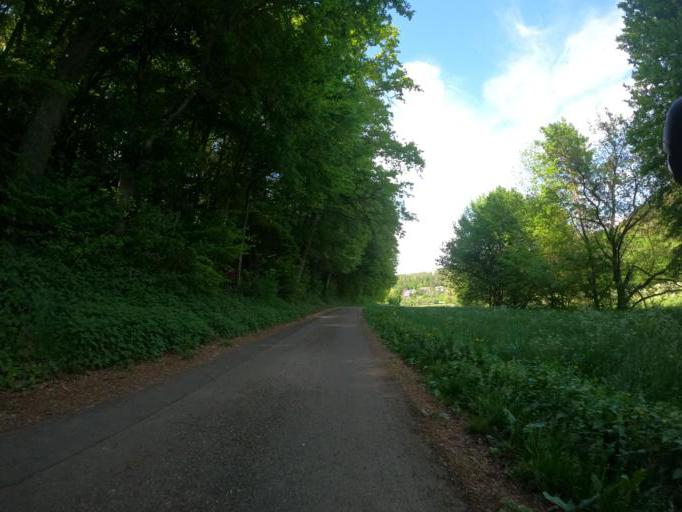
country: DE
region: Baden-Wuerttemberg
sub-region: Regierungsbezirk Stuttgart
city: Aidlingen
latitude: 48.6755
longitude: 8.9101
